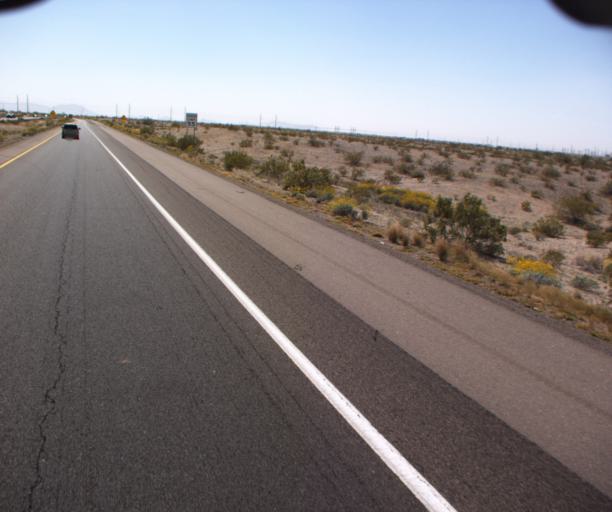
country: US
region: Arizona
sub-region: Maricopa County
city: Gila Bend
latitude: 32.9825
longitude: -112.6678
